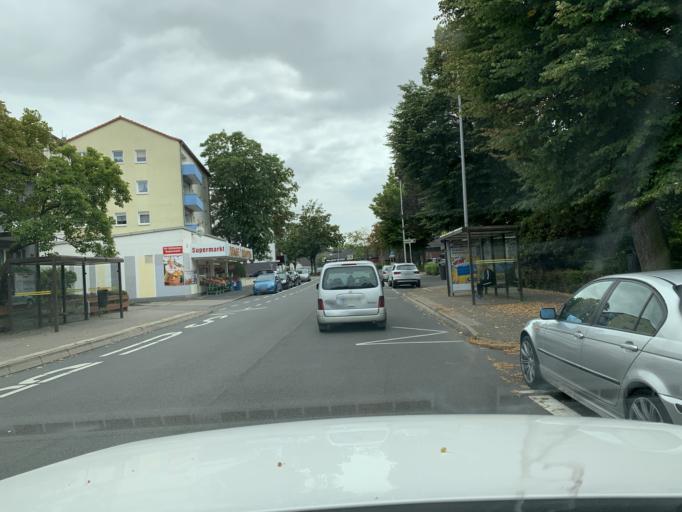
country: DE
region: North Rhine-Westphalia
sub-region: Regierungsbezirk Dusseldorf
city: Oberhausen
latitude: 51.4594
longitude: 6.8994
